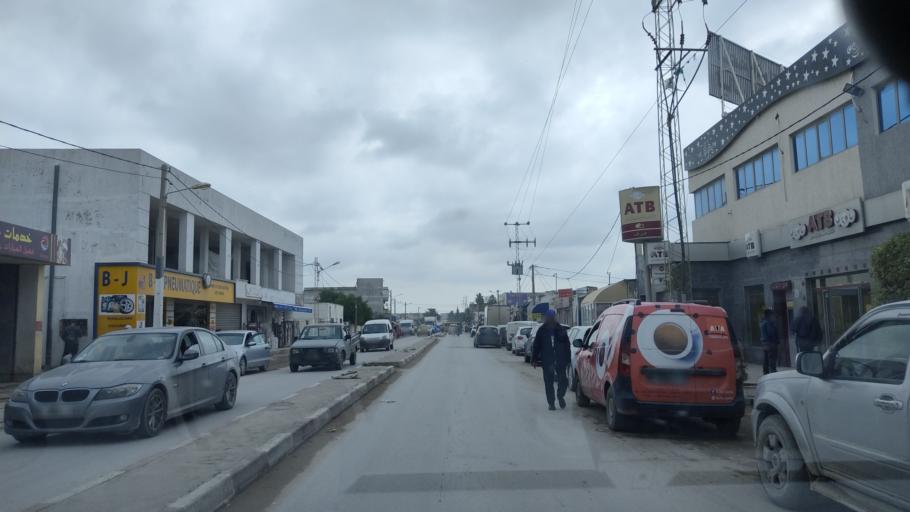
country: TN
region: Ariana
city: Ariana
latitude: 36.8867
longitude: 10.2177
